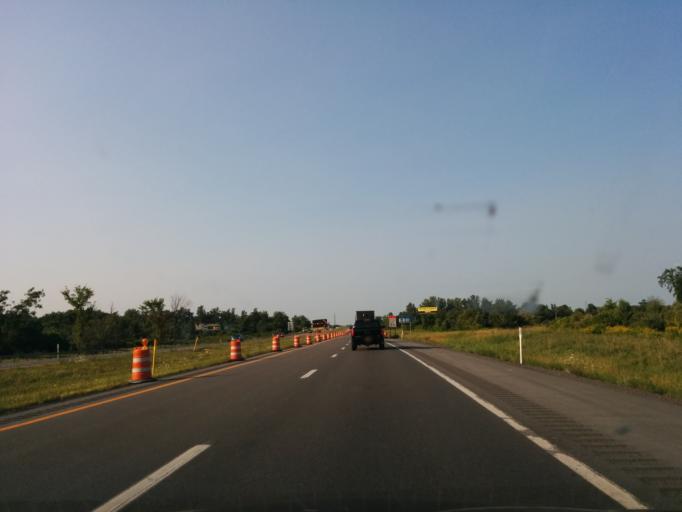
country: US
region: New York
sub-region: Jefferson County
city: Adams Center
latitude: 43.9046
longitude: -75.9812
